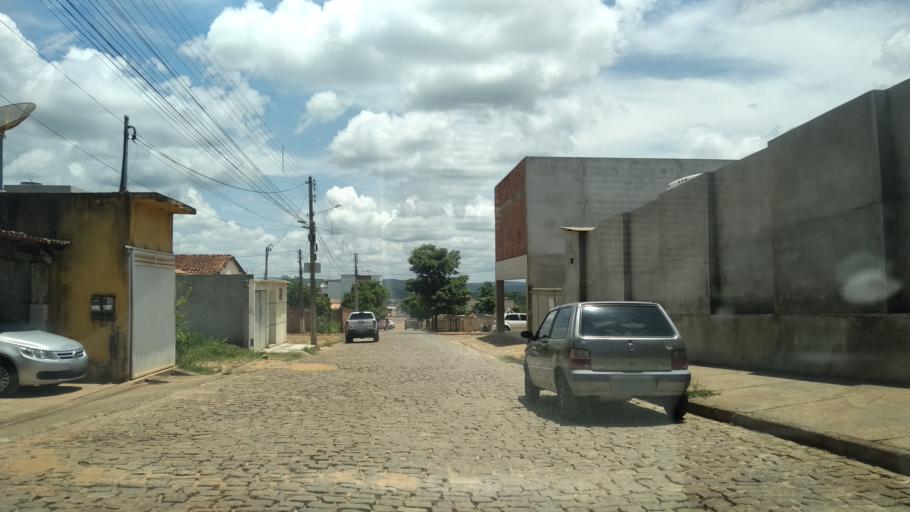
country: BR
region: Bahia
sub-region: Caetite
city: Caetite
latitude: -14.0615
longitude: -42.4859
